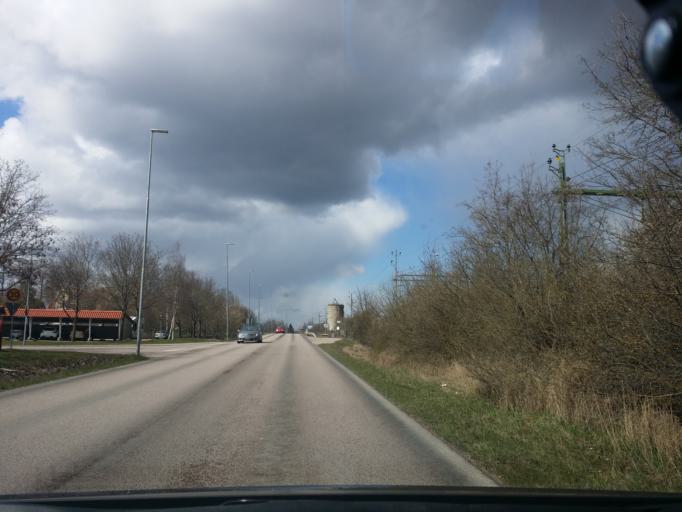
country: SE
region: Vaestmanland
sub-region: Sala Kommun
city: Sala
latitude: 59.9273
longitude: 16.5988
